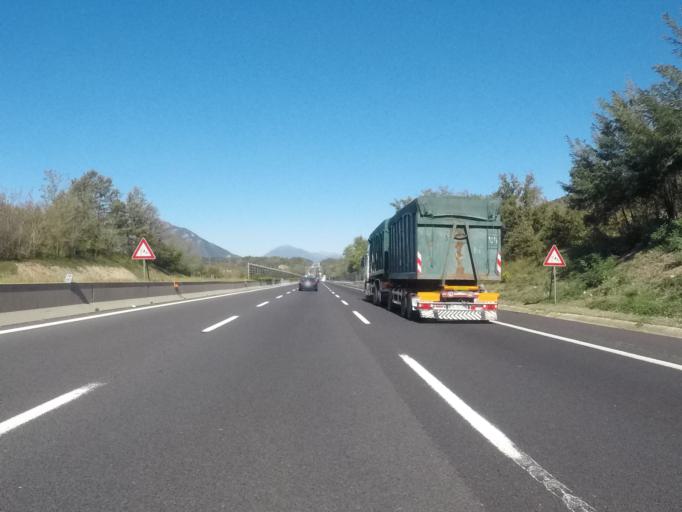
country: IT
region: Campania
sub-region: Provincia di Caserta
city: Tora
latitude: 41.3538
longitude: 14.0402
